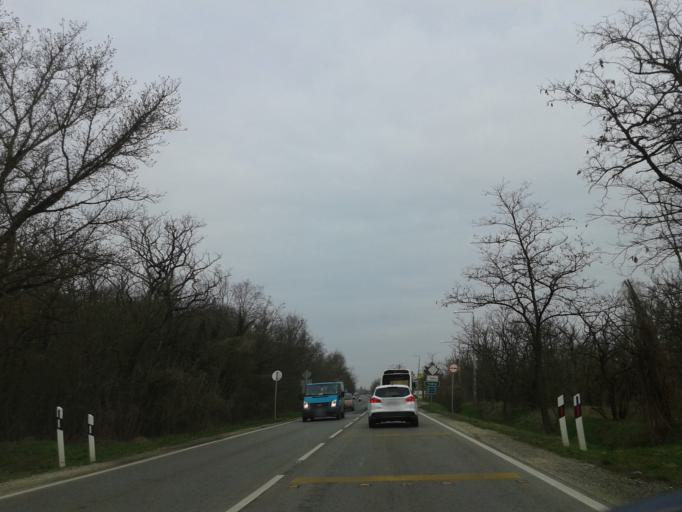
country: HU
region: Komarom-Esztergom
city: Baj
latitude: 47.6344
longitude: 18.3530
